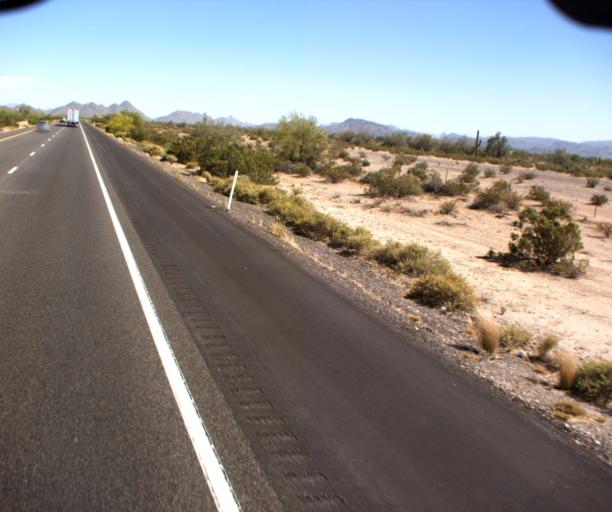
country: US
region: Arizona
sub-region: Maricopa County
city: Gila Bend
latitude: 32.9138
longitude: -112.6194
